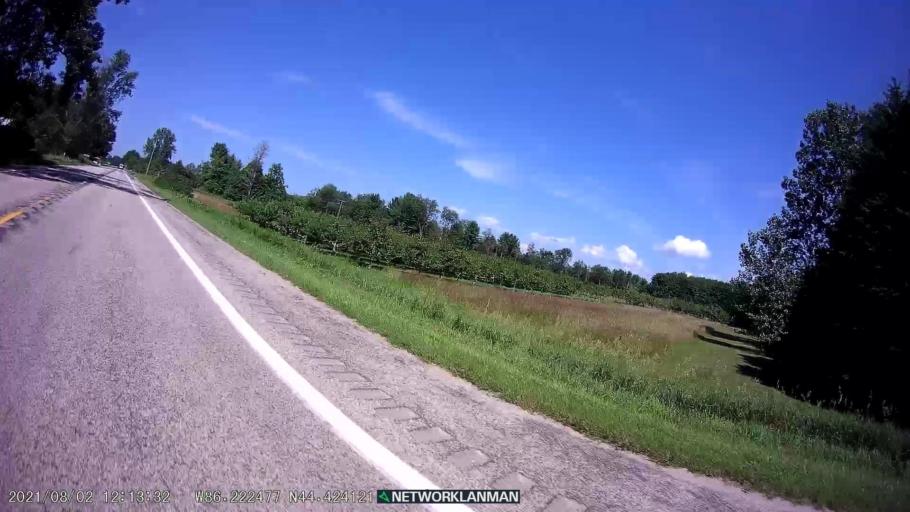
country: US
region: Michigan
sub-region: Manistee County
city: Manistee
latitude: 44.4242
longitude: -86.2225
